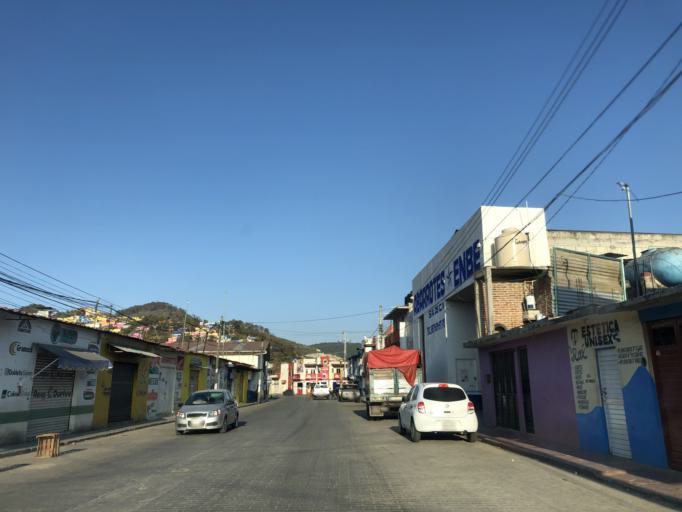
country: MX
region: Chiapas
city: San Cristobal de las Casas
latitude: 16.7187
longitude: -92.6380
